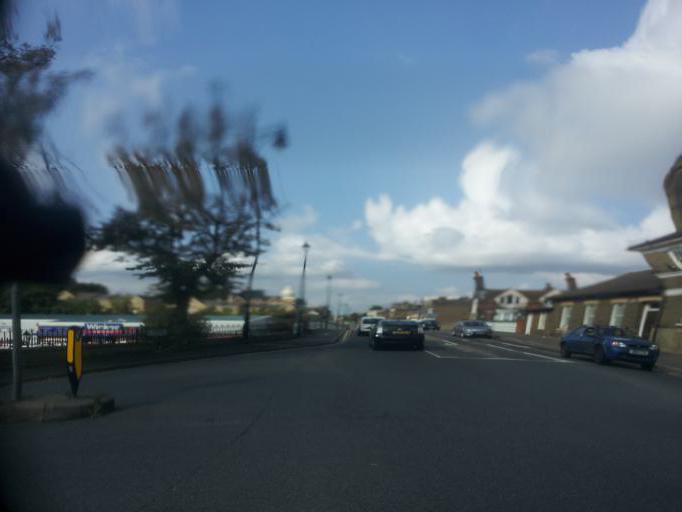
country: GB
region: England
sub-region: Kent
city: Chatham
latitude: 51.3814
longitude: 0.5229
